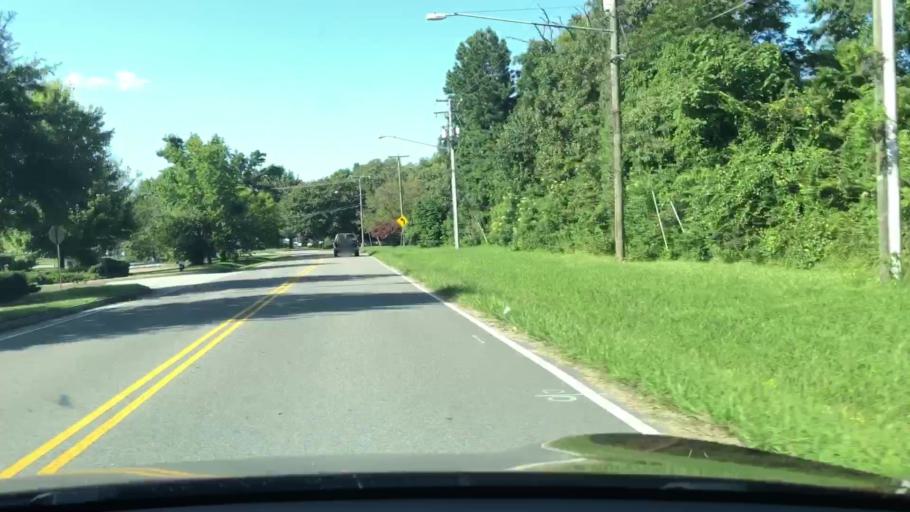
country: US
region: Virginia
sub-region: City of Virginia Beach
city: Virginia Beach
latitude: 36.8451
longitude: -76.0354
